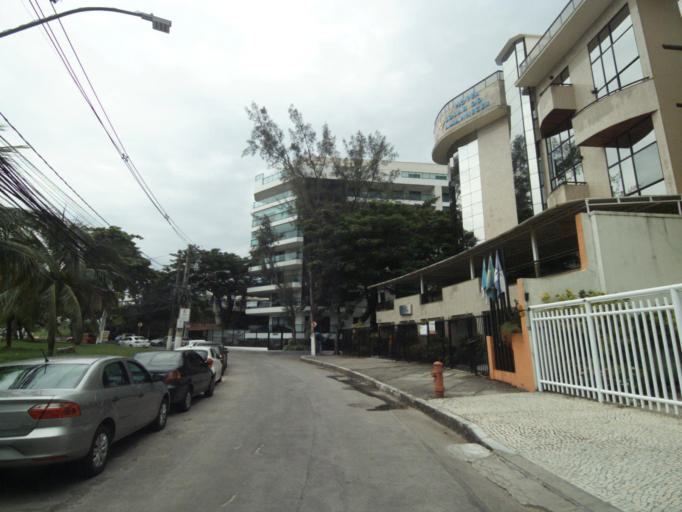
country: BR
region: Rio de Janeiro
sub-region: Niteroi
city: Niteroi
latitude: -22.9311
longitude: -43.0974
